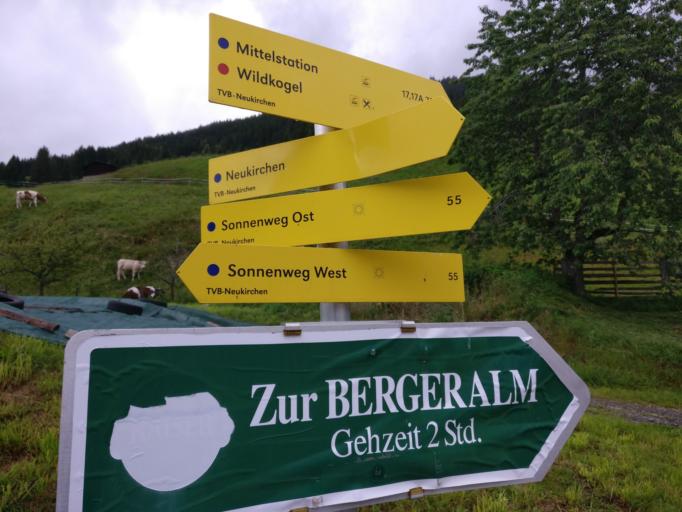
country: AT
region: Salzburg
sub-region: Politischer Bezirk Zell am See
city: Neukirchen am Grossvenediger
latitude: 47.2604
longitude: 12.2792
